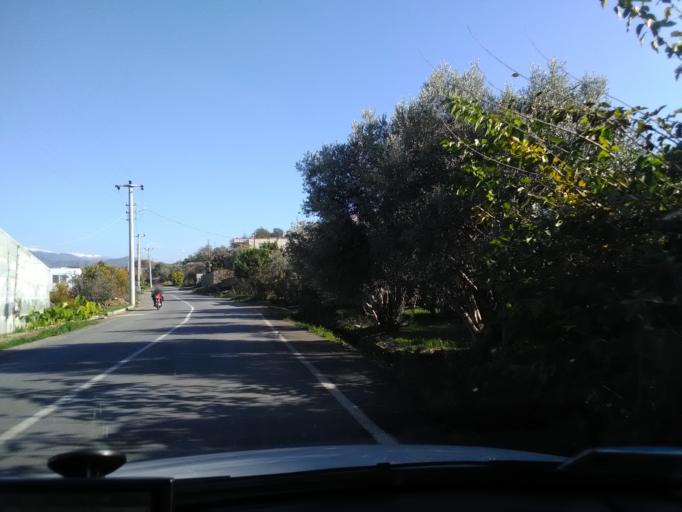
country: TR
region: Antalya
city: Gazipasa
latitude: 36.2588
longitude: 32.3094
